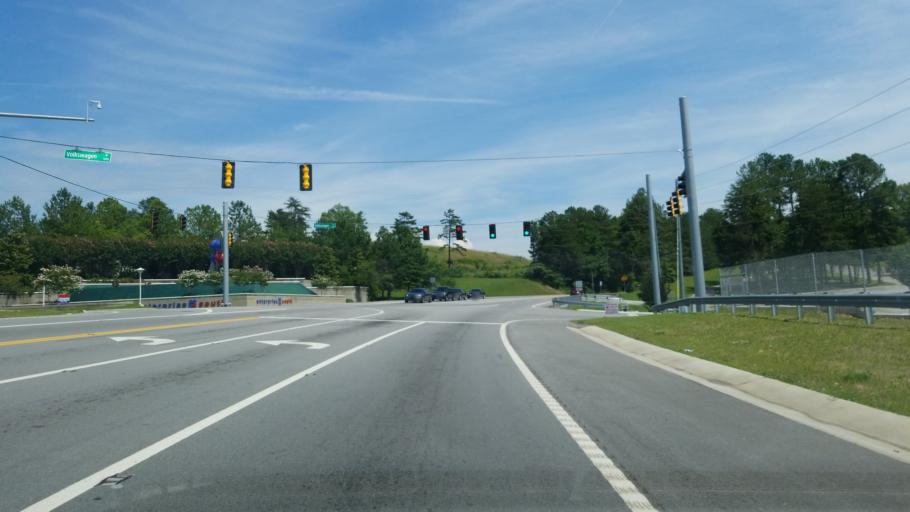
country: US
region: Tennessee
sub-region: Hamilton County
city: Harrison
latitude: 35.0688
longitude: -85.1478
